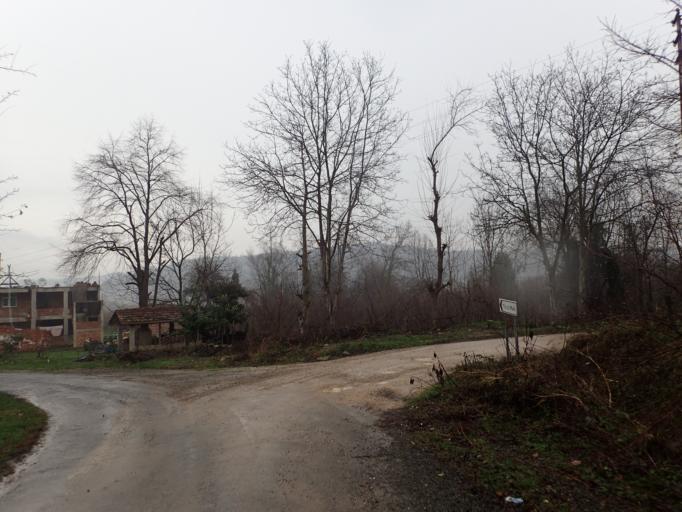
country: TR
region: Ordu
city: Camas
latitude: 40.9510
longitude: 37.5097
